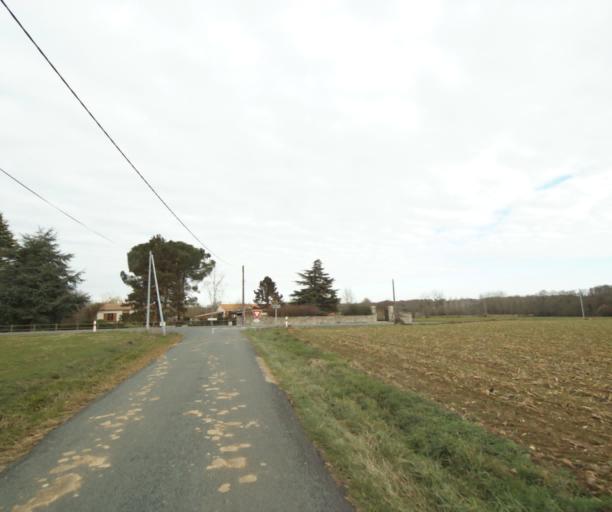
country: FR
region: Poitou-Charentes
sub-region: Departement de la Charente-Maritime
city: Corme-Royal
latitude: 45.7356
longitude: -0.7794
